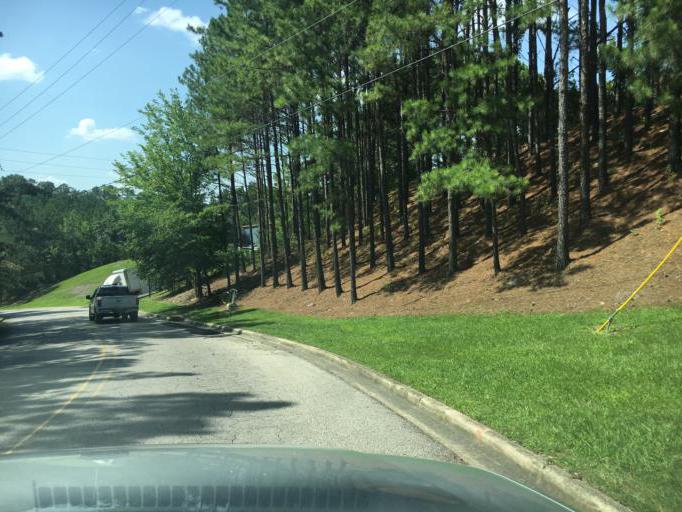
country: US
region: Alabama
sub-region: Shelby County
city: Meadowbrook
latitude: 33.4279
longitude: -86.7121
